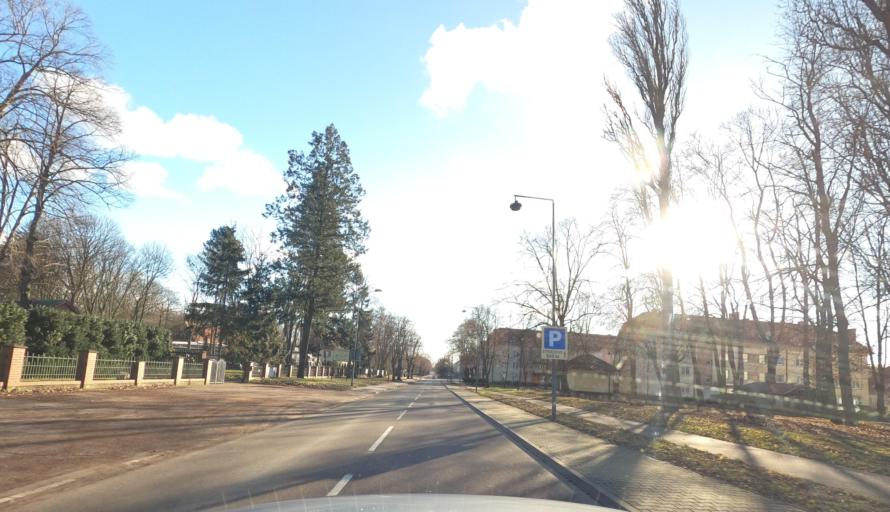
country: PL
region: West Pomeranian Voivodeship
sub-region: Powiat pyrzycki
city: Warnice
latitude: 53.2959
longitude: 14.9936
